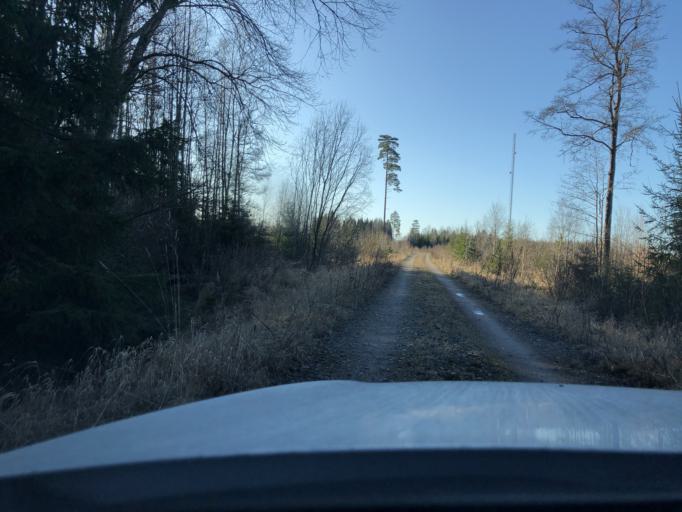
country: SE
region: Gaevleborg
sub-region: Gavle Kommun
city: Hedesunda
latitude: 60.3009
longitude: 16.8914
